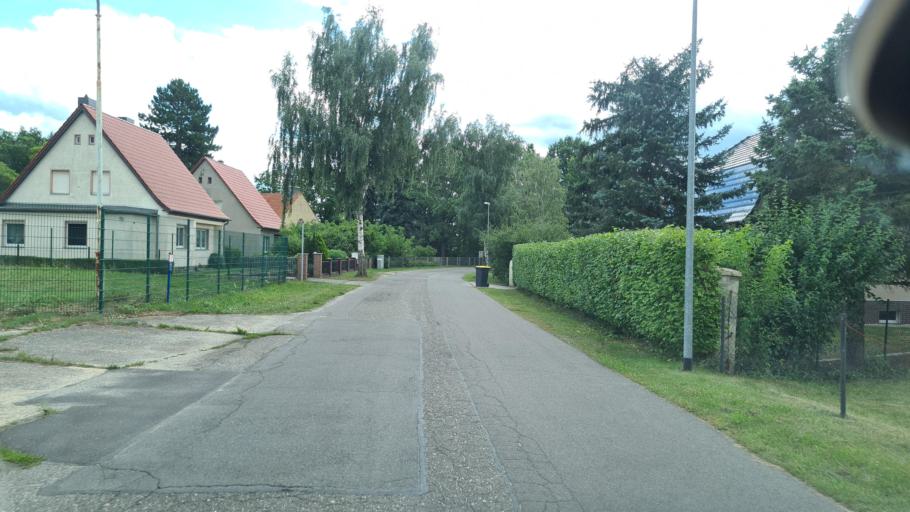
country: DE
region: Brandenburg
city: Drebkau
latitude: 51.6488
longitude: 14.2253
